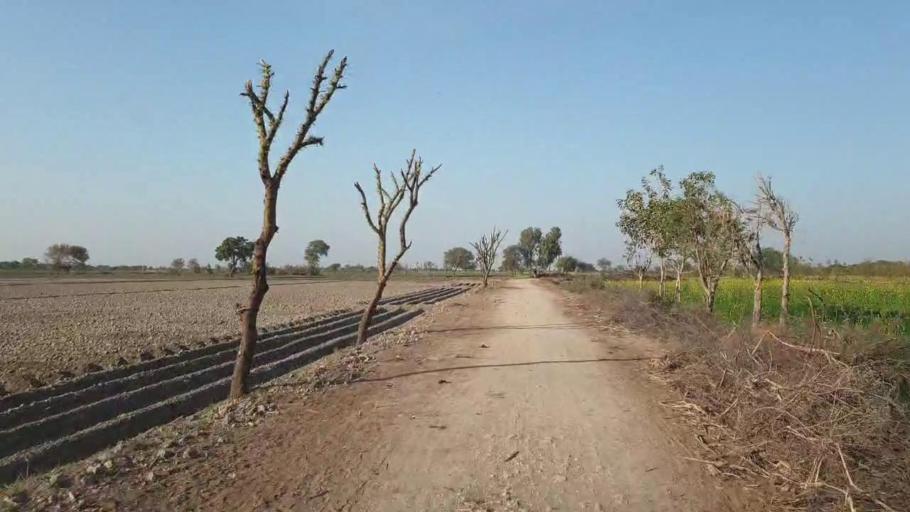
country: PK
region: Sindh
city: Tando Allahyar
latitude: 25.3767
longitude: 68.6979
